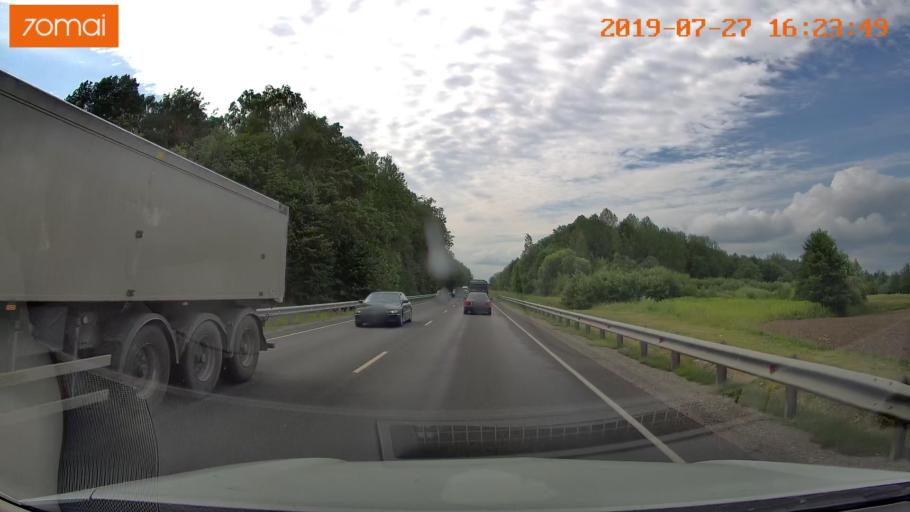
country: RU
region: Kaliningrad
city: Zheleznodorozhnyy
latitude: 54.6322
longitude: 21.4655
